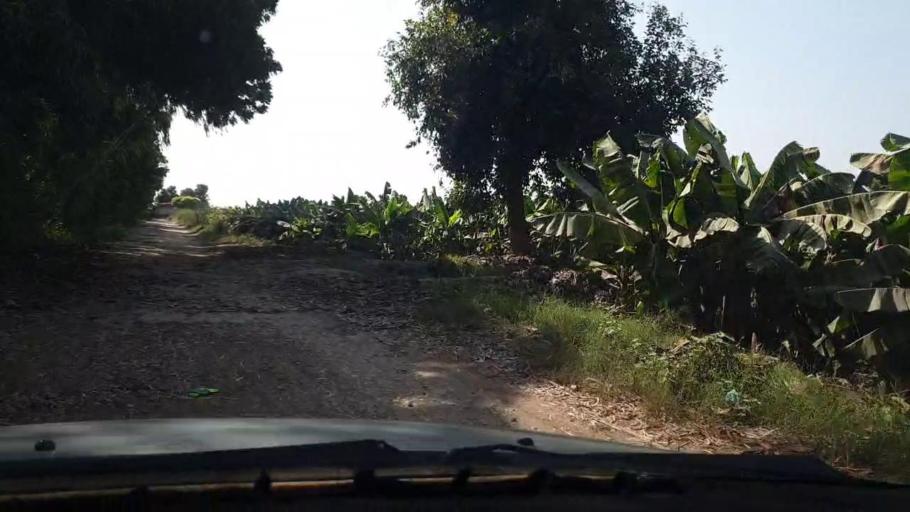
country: PK
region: Sindh
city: Chambar
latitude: 25.2445
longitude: 68.9083
